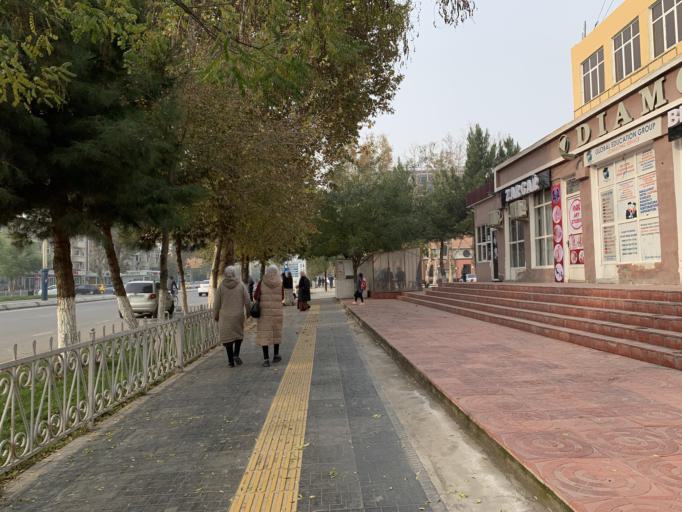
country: UZ
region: Fergana
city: Qo`qon
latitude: 40.5459
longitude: 70.9297
